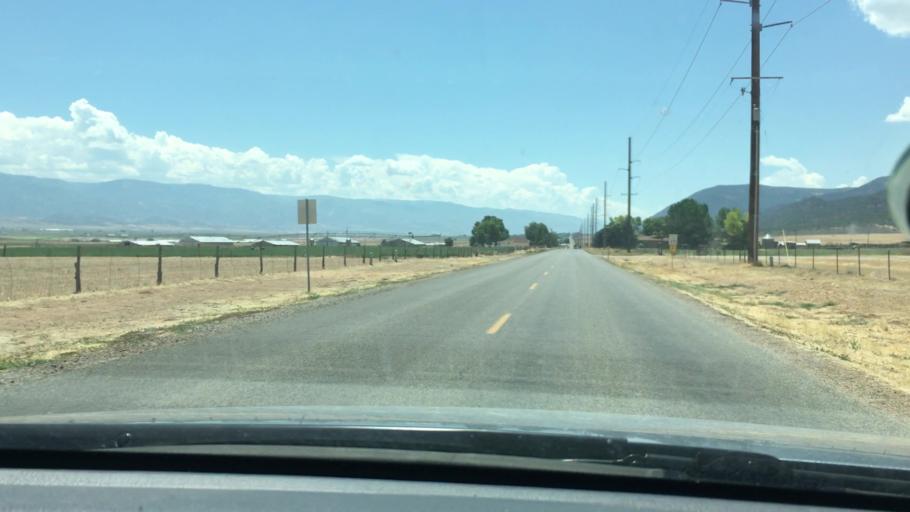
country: US
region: Utah
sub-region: Sanpete County
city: Moroni
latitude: 39.5463
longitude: -111.6401
